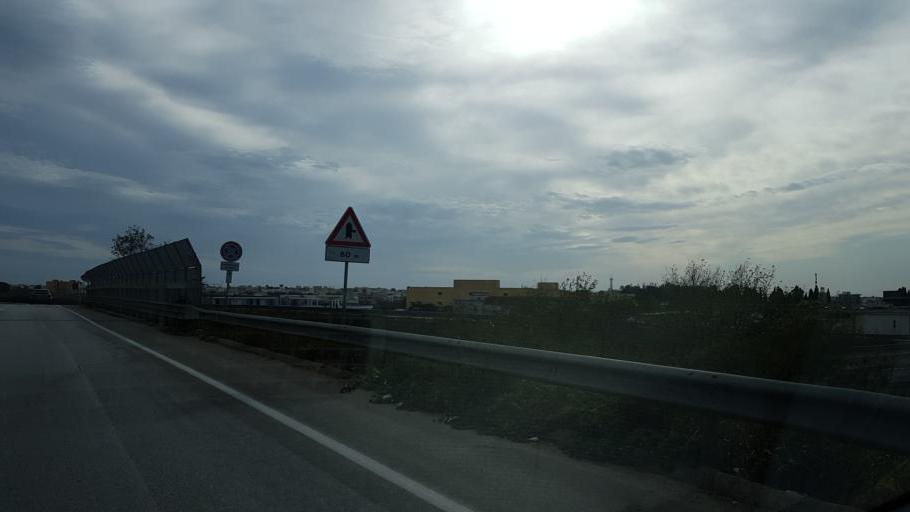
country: IT
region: Apulia
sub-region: Provincia di Brindisi
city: Mesagne
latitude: 40.5694
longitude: 17.8199
